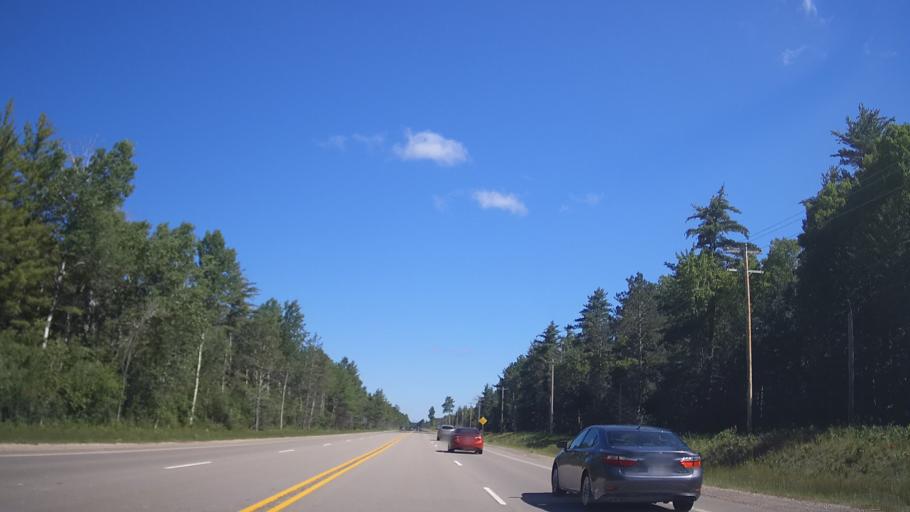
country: US
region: Michigan
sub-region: Cheboygan County
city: Indian River
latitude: 45.5193
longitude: -84.7816
